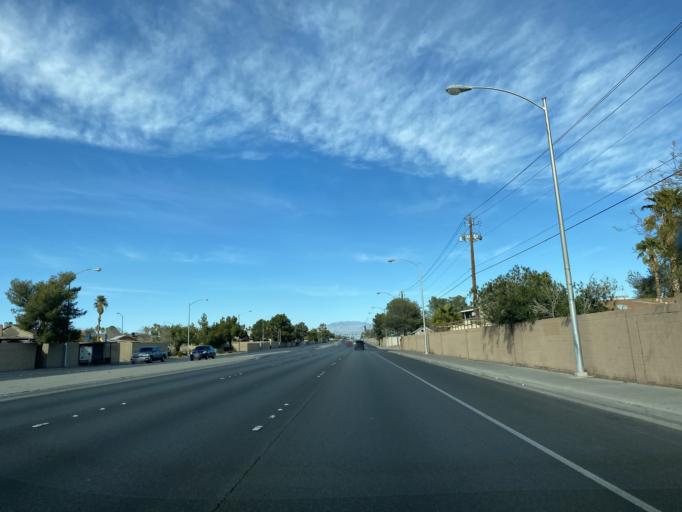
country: US
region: Nevada
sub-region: Clark County
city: Spring Valley
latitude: 36.1172
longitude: -115.2428
